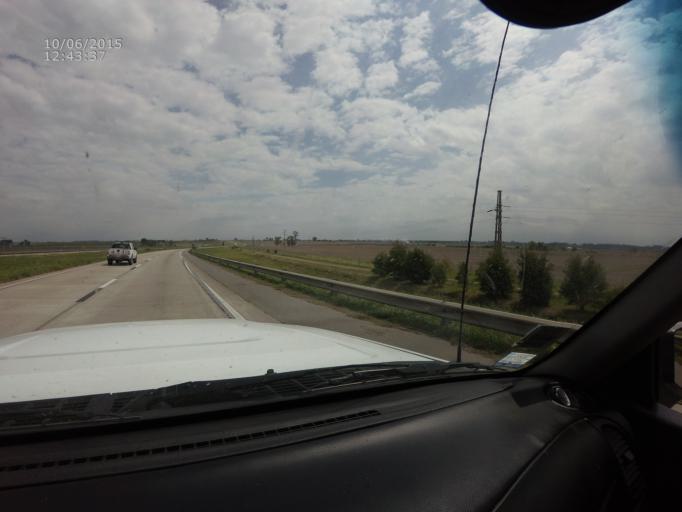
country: AR
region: Santa Fe
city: Canada de Gomez
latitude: -32.8544
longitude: -61.3511
